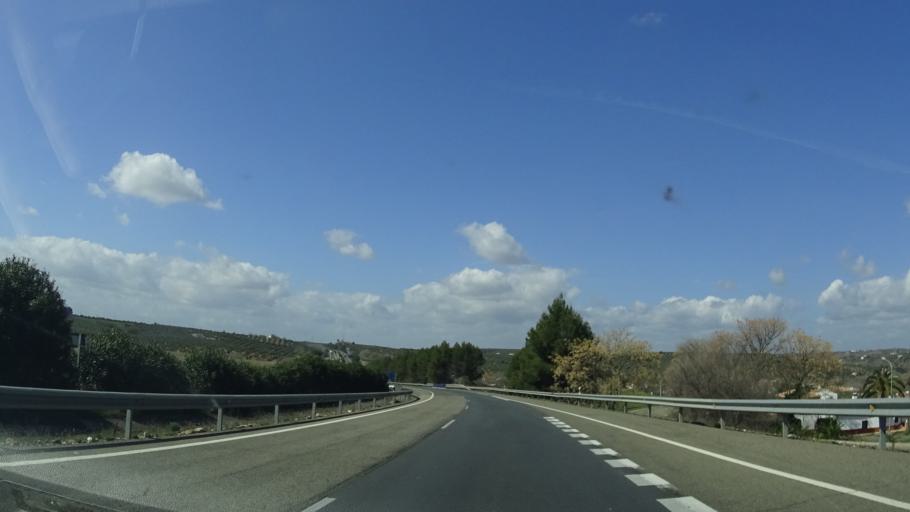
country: ES
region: Andalusia
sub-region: Province of Cordoba
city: Montoro
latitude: 38.0053
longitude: -4.3480
